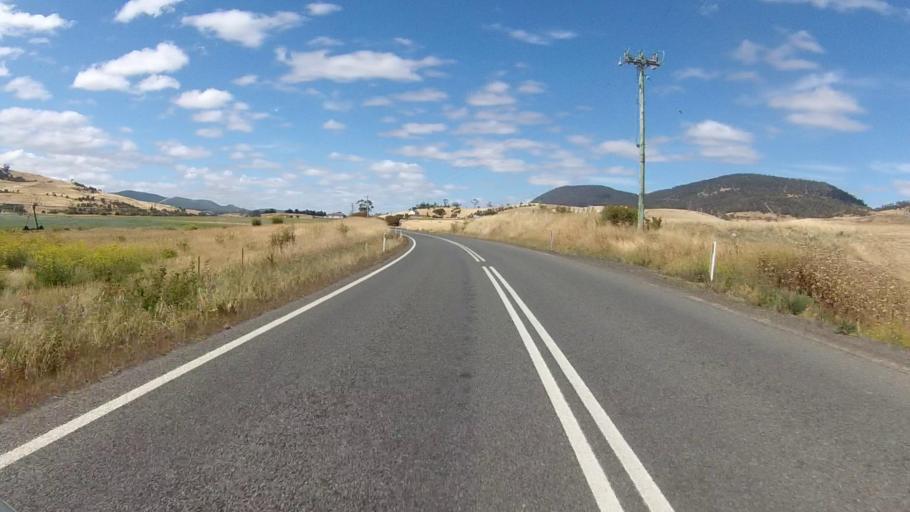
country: AU
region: Tasmania
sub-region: Brighton
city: Bridgewater
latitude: -42.5872
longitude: 147.4083
